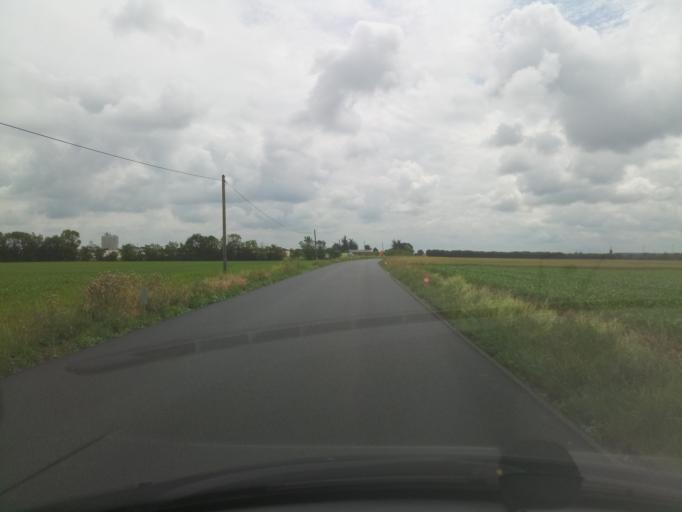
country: FR
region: Poitou-Charentes
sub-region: Departement de la Charente-Maritime
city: Saint-Jean-de-Liversay
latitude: 46.2701
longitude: -0.8900
